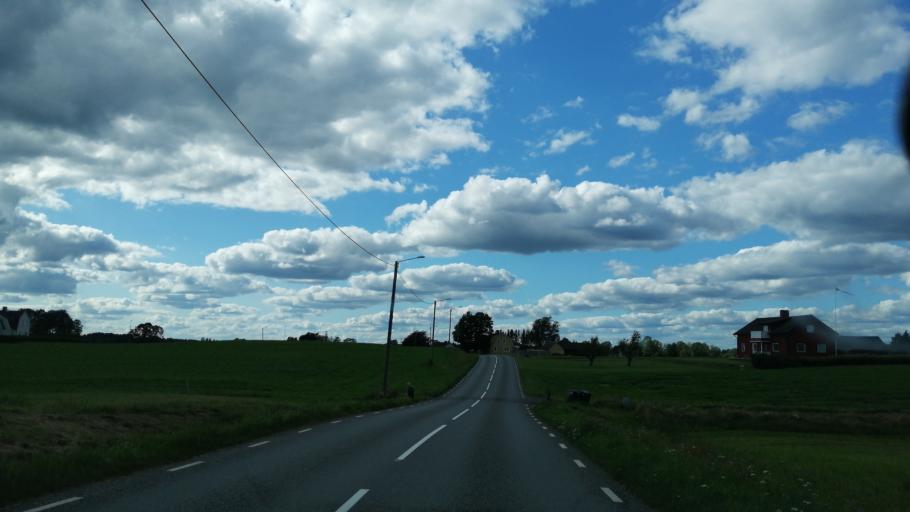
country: SE
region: Joenkoeping
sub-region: Gislaveds Kommun
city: Reftele
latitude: 57.1643
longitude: 13.6165
